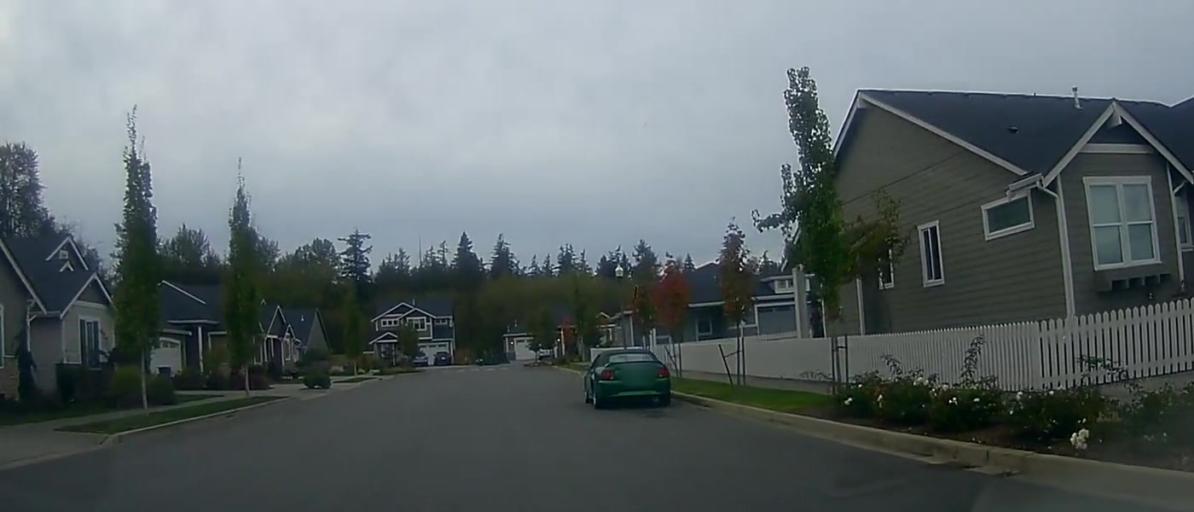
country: US
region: Washington
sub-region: Skagit County
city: Burlington
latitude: 48.4470
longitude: -122.3009
